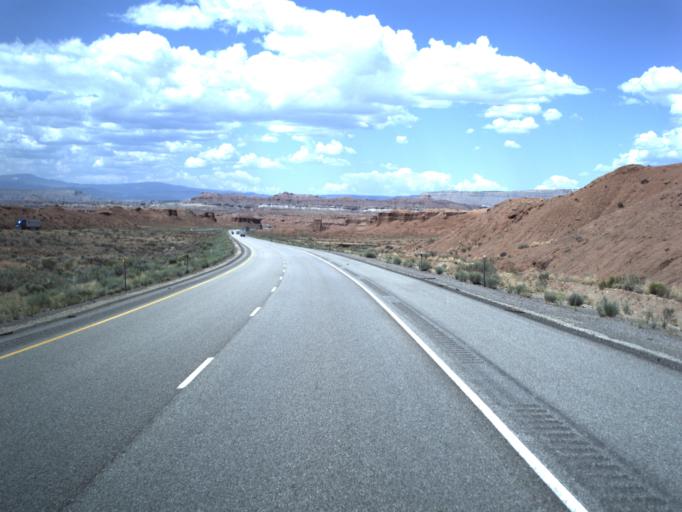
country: US
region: Utah
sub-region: Emery County
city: Ferron
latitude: 38.8477
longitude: -111.0310
